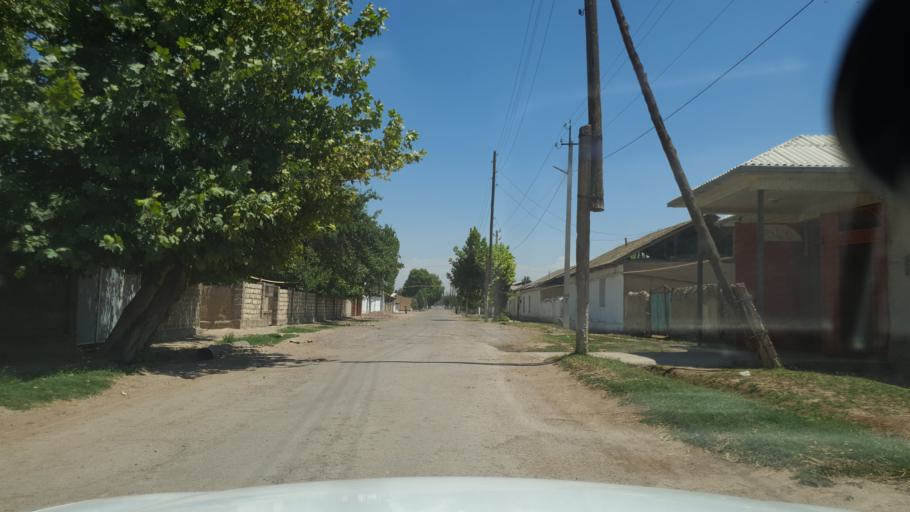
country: UZ
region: Toshkent
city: Piskent
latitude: 40.8268
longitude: 69.4073
